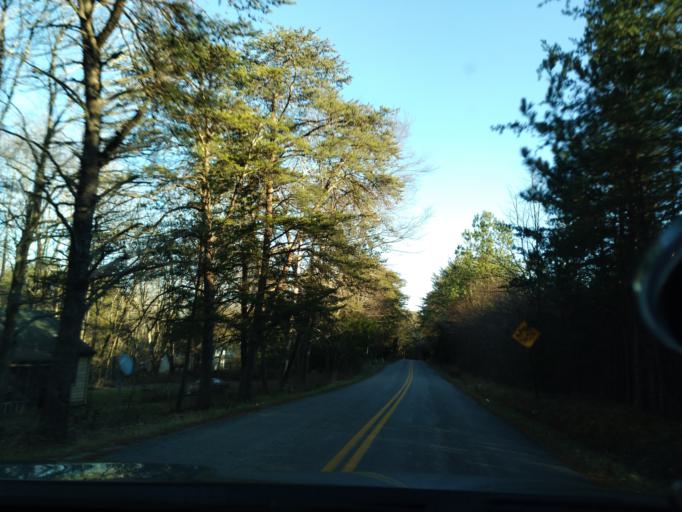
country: US
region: Virginia
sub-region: Prince Edward County
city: Hampden Sydney
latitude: 37.3222
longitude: -78.5753
